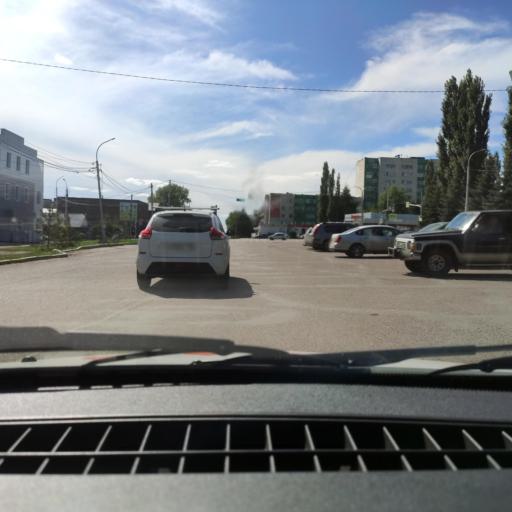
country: RU
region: Bashkortostan
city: Blagoveshchensk
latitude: 55.0459
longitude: 55.9603
